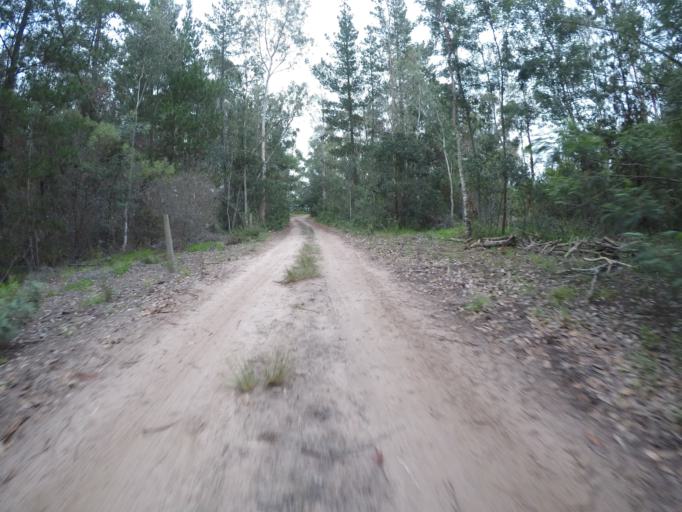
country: ZA
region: Western Cape
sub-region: Eden District Municipality
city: Knysna
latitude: -34.0059
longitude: 22.7953
